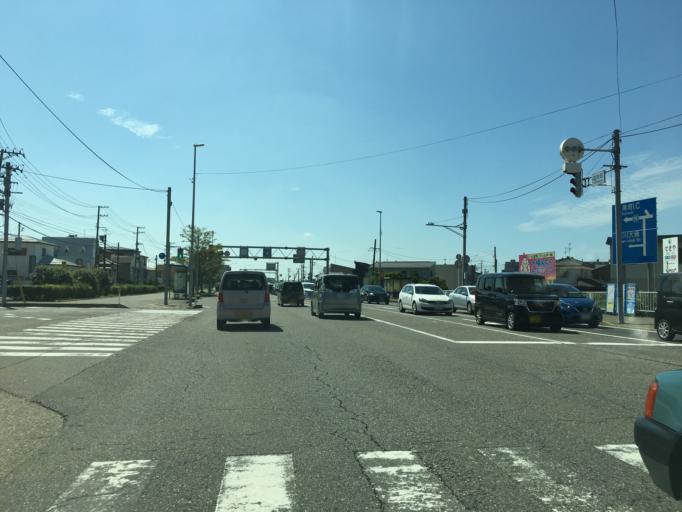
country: JP
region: Niigata
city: Niigata-shi
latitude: 37.9014
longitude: 139.0144
